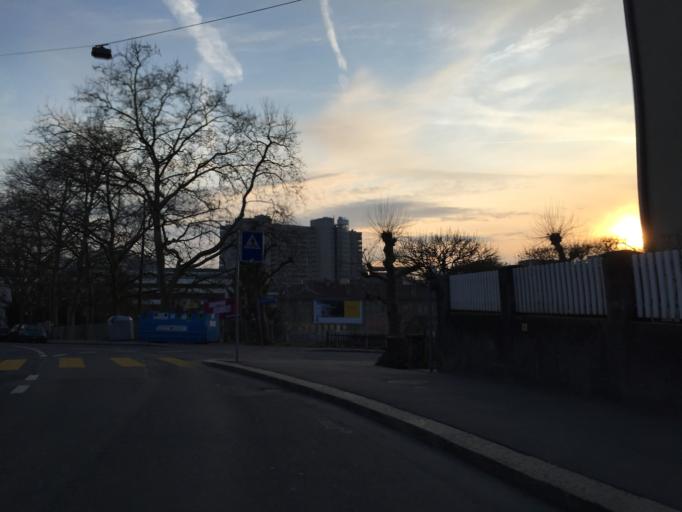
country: CH
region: Bern
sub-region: Bern-Mittelland District
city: Bern
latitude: 46.9503
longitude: 7.4288
